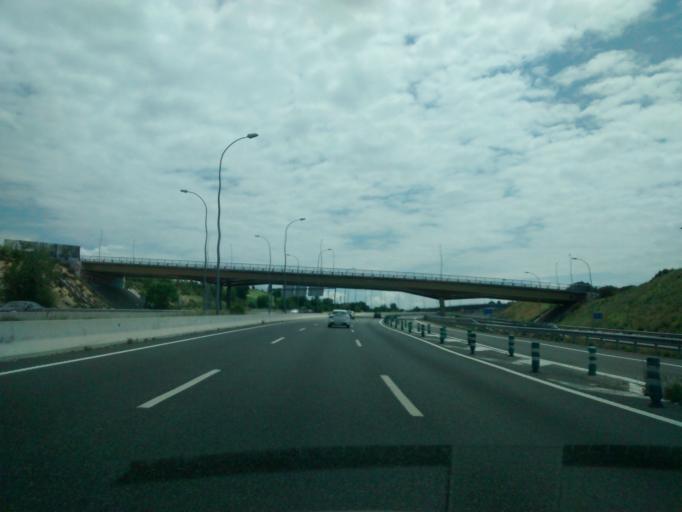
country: ES
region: Madrid
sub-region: Provincia de Madrid
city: Hortaleza
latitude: 40.4910
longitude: -3.6447
